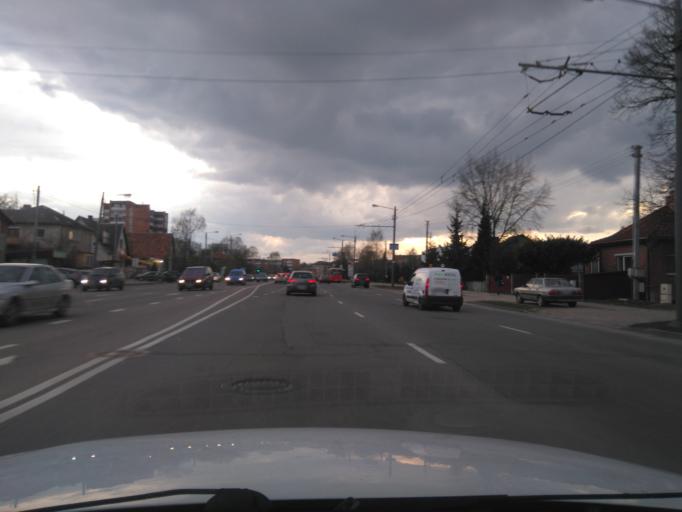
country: LT
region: Kauno apskritis
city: Dainava (Kaunas)
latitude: 54.9113
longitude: 23.9453
